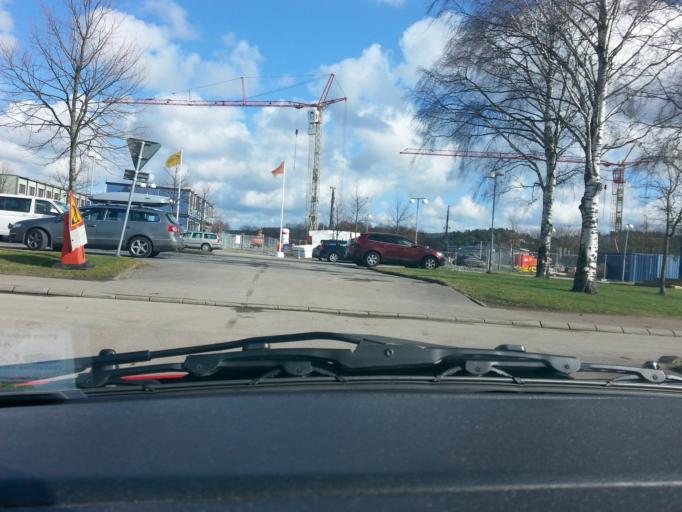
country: SE
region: Vaestra Goetaland
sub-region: Partille Kommun
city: Partille
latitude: 57.7402
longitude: 12.1140
